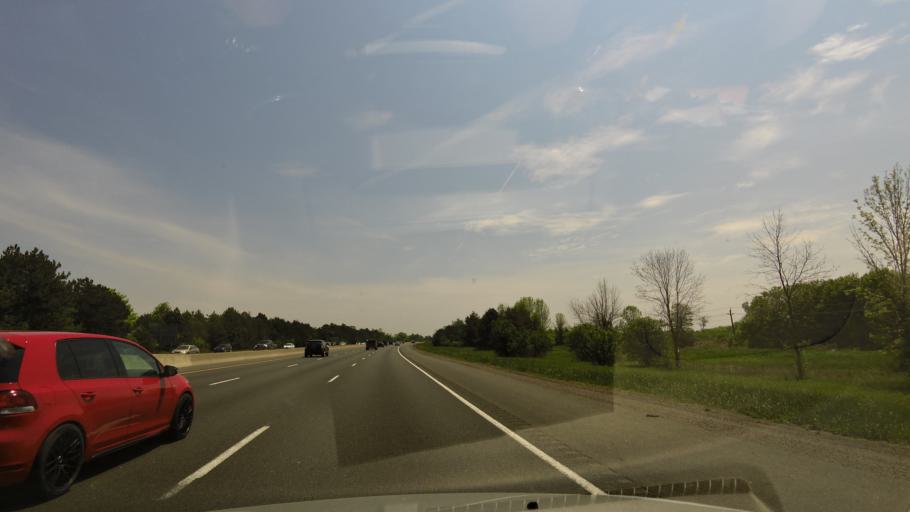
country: CA
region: Ontario
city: Oshawa
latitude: 43.8845
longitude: -78.8131
